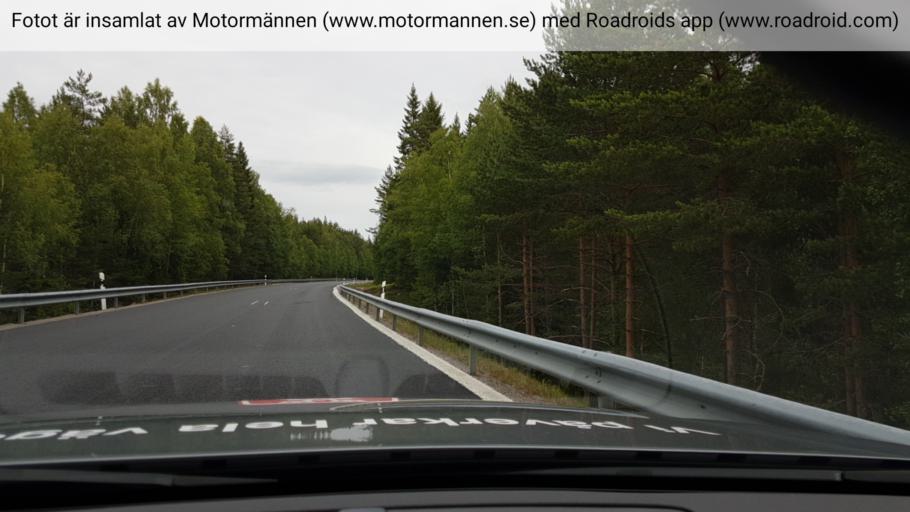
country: SE
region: Vaestmanland
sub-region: Skinnskattebergs Kommun
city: Skinnskatteberg
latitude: 59.8606
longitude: 15.5929
